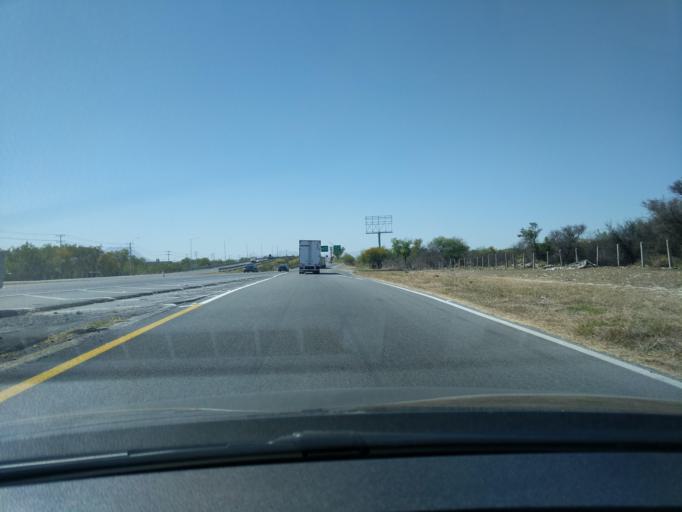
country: MX
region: Nuevo Leon
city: Juarez
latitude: 25.6574
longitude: -100.0746
